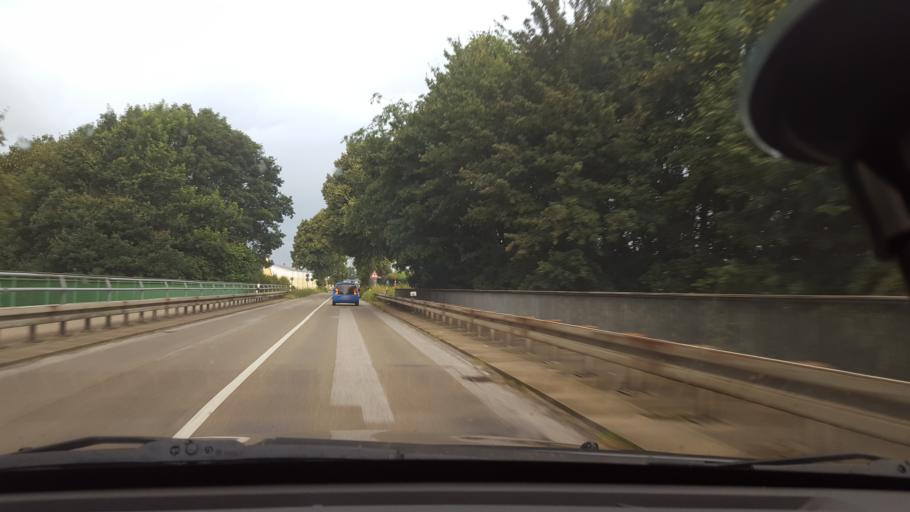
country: DE
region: North Rhine-Westphalia
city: Herten
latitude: 51.6527
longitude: 7.1502
